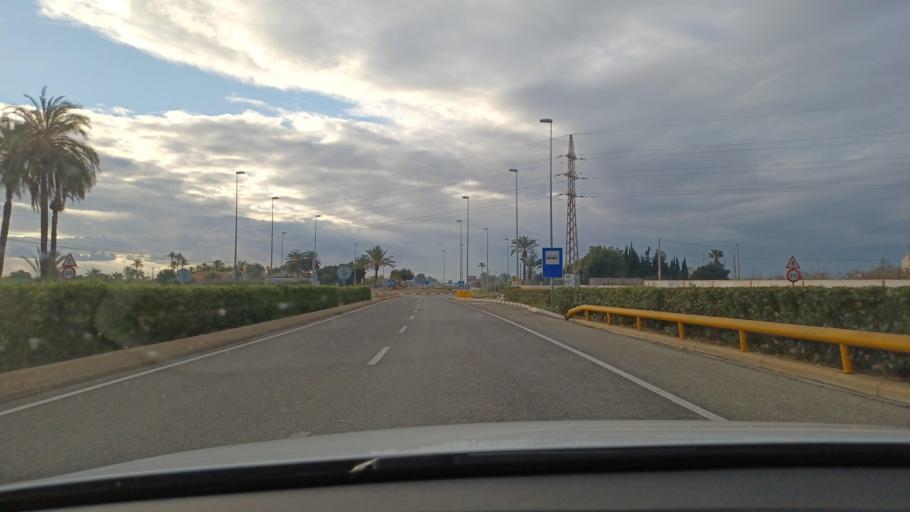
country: ES
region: Valencia
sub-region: Provincia de Alicante
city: Elche
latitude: 38.2330
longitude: -0.7004
